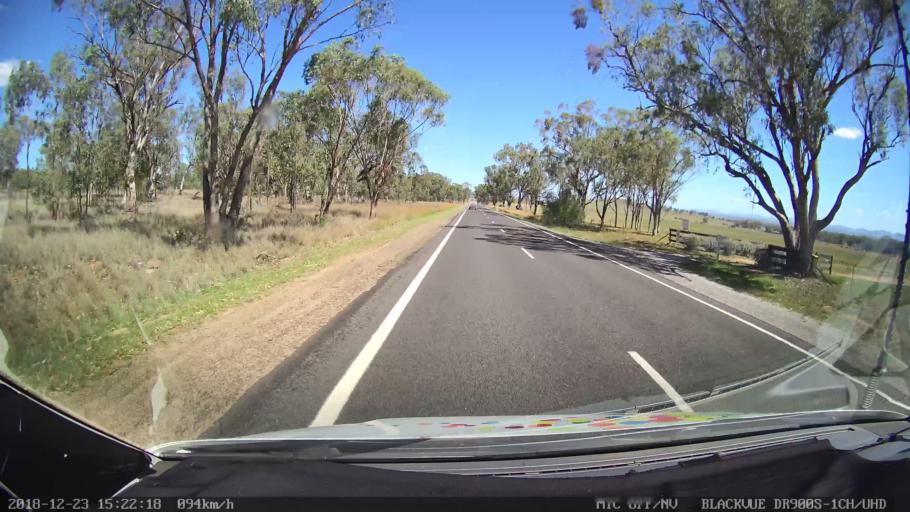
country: AU
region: New South Wales
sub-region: Tamworth Municipality
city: Manilla
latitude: -30.8667
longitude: 150.8036
